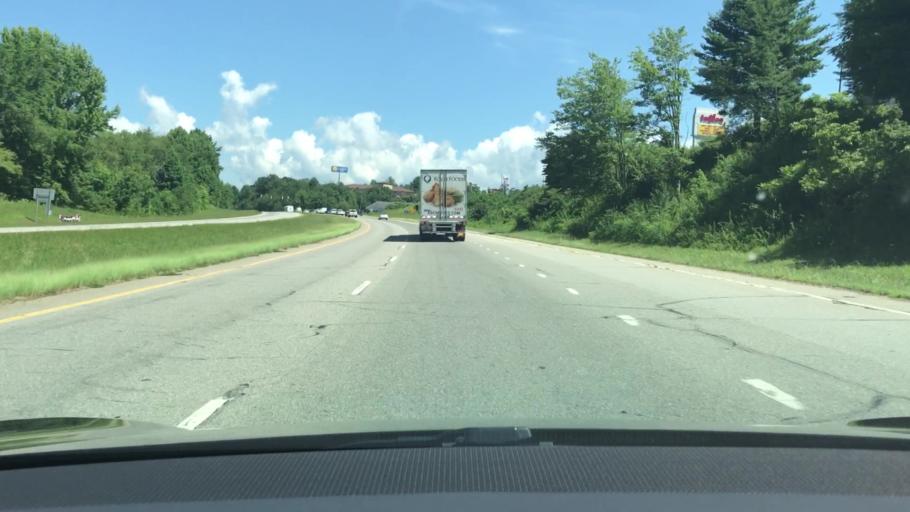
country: US
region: North Carolina
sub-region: Macon County
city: Franklin
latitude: 35.1797
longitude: -83.3566
